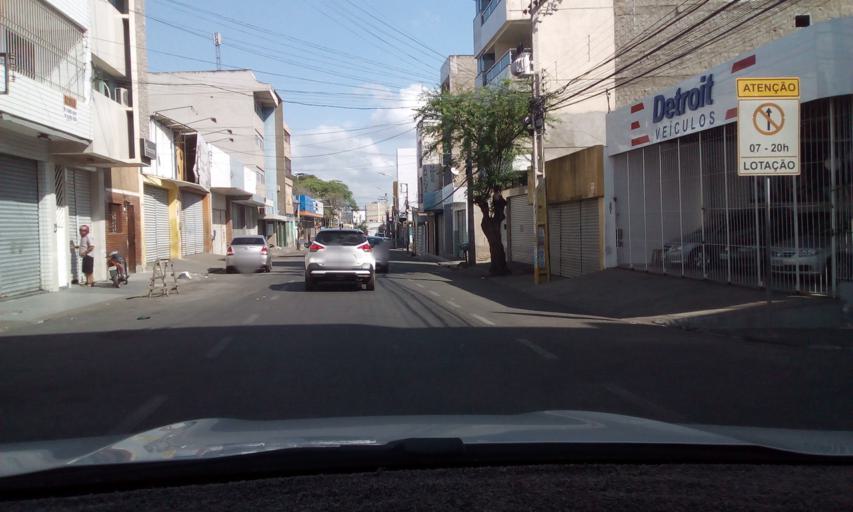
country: BR
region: Pernambuco
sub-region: Caruaru
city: Caruaru
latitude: -8.2787
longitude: -35.9742
